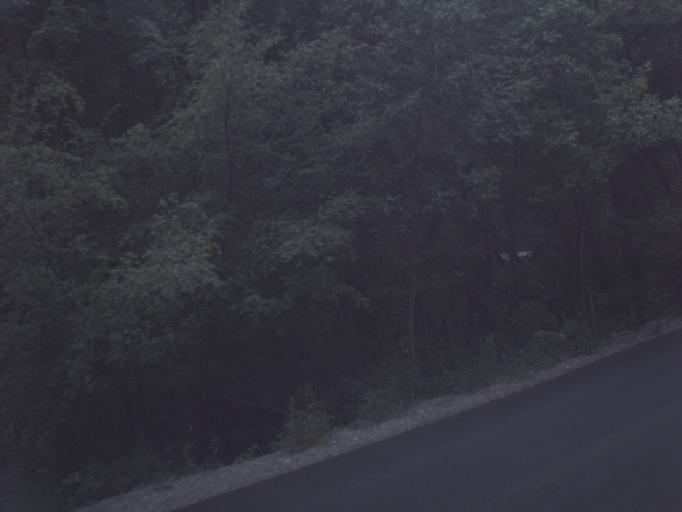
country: US
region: Utah
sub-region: Utah County
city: Cedar Hills
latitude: 40.4525
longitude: -111.6590
